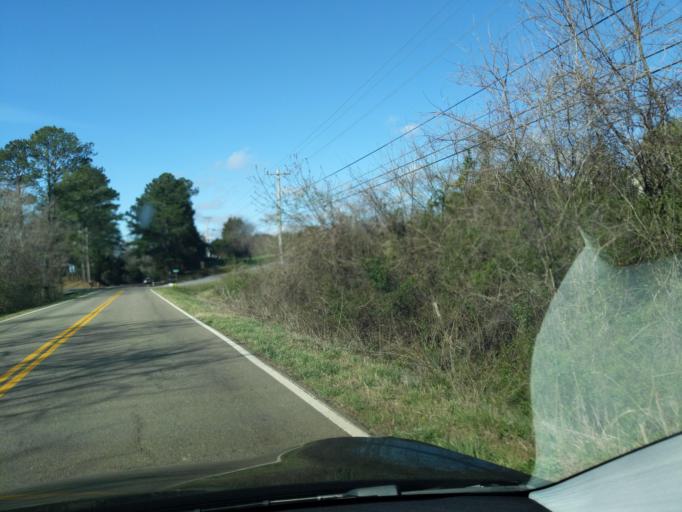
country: US
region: Tennessee
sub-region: Jefferson County
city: Dandridge
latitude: 35.9752
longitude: -83.4922
